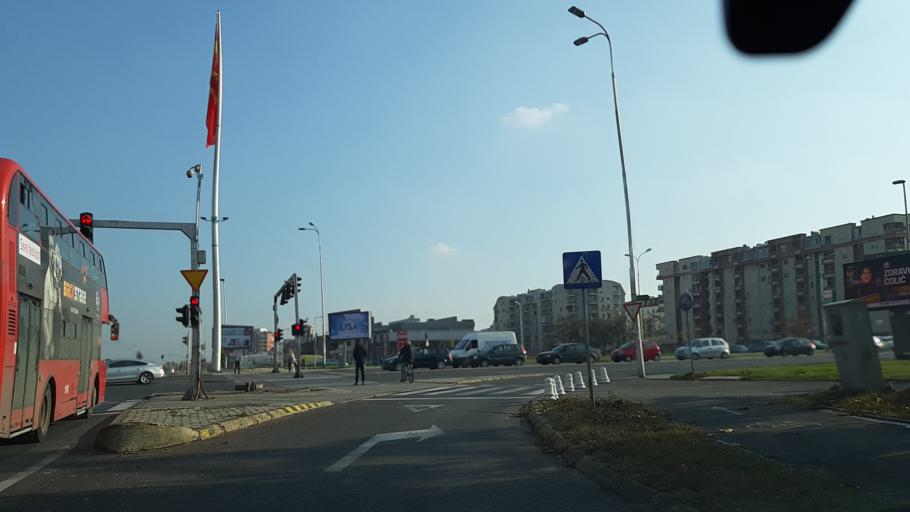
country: MK
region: Kisela Voda
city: Usje
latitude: 41.9826
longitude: 21.4708
